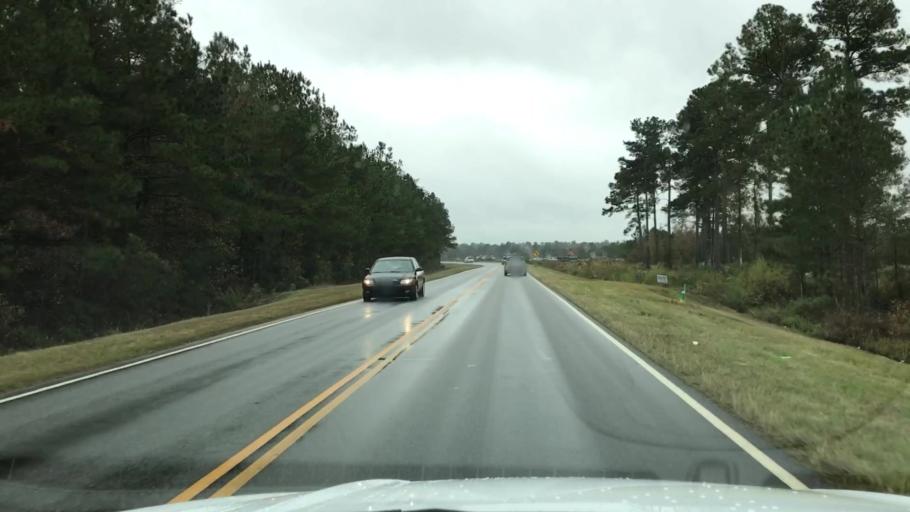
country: US
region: South Carolina
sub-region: Horry County
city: Myrtle Beach
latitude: 33.7578
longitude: -78.8838
